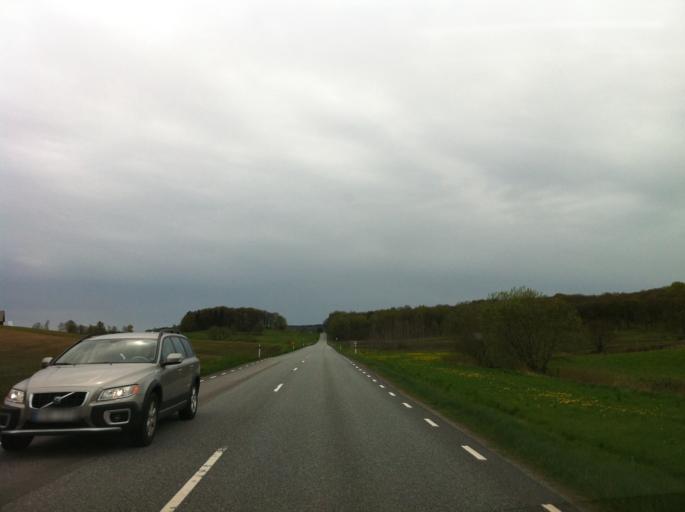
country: SE
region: Halland
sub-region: Falkenbergs Kommun
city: Falkenberg
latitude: 57.0412
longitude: 12.6033
